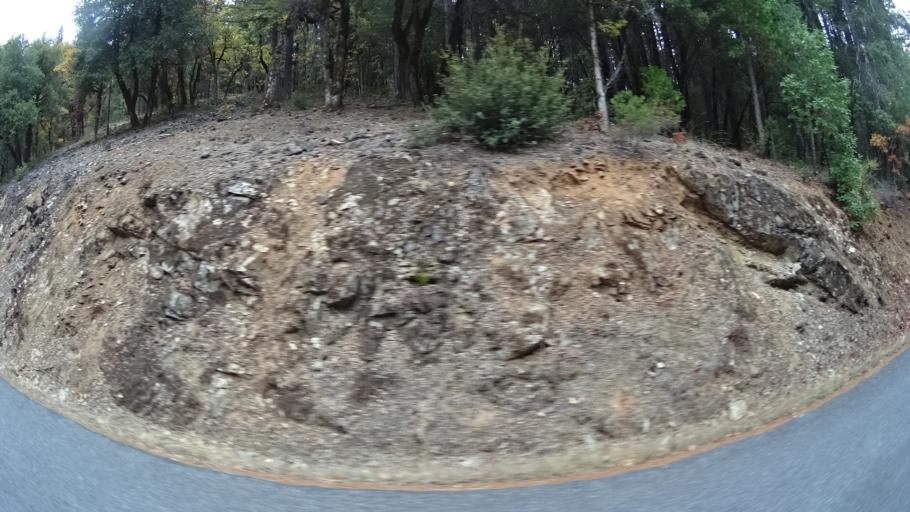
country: US
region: California
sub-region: Siskiyou County
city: Happy Camp
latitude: 41.7511
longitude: -123.3629
